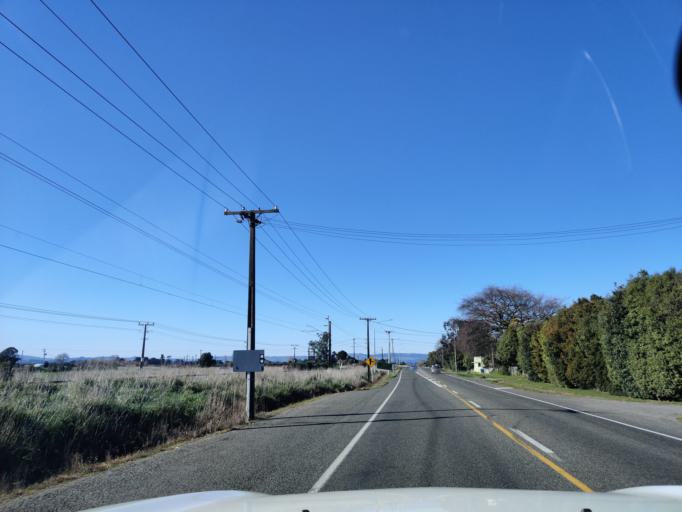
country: NZ
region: Manawatu-Wanganui
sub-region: Palmerston North City
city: Palmerston North
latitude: -40.2432
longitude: 175.5845
